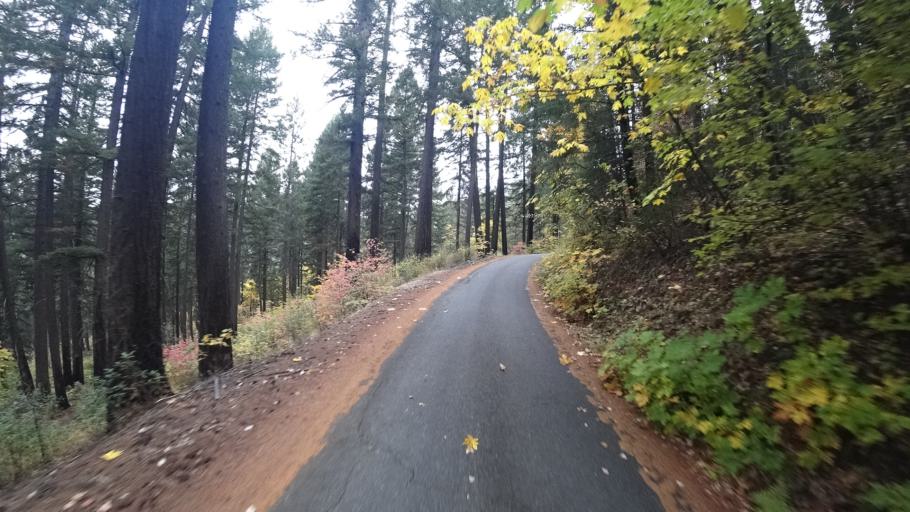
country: US
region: California
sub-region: Siskiyou County
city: Happy Camp
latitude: 41.8194
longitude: -123.3324
